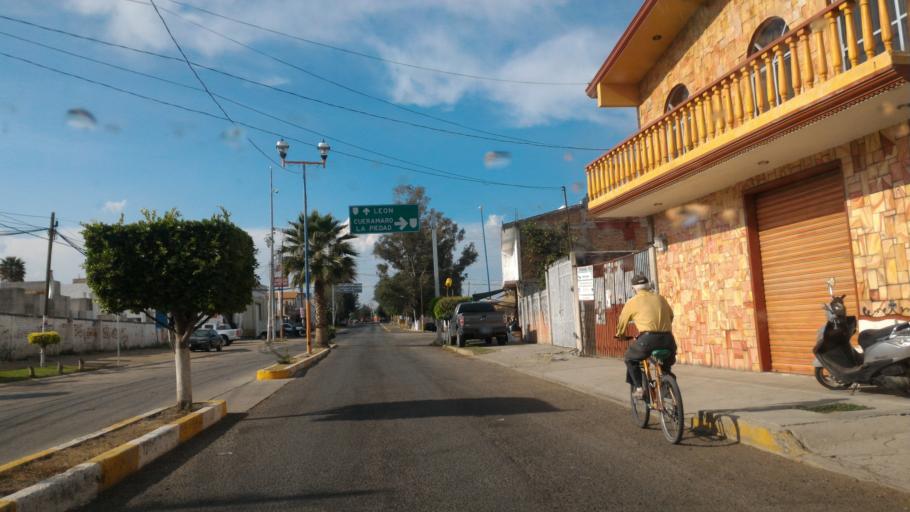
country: MX
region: Guanajuato
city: Ciudad Manuel Doblado
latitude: 20.7334
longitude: -101.9518
